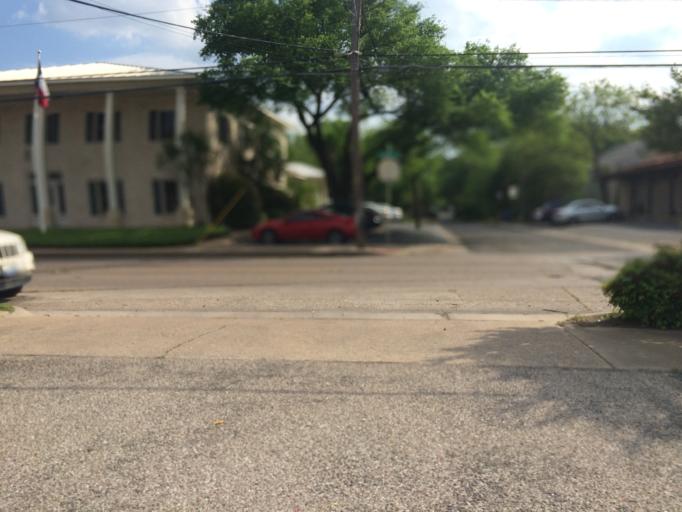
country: US
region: Texas
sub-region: Travis County
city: Austin
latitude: 30.3016
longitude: -97.7420
